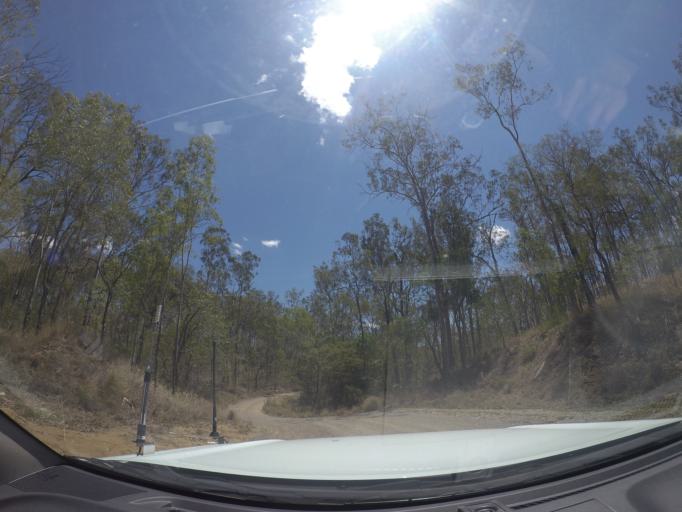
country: AU
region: Queensland
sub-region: Ipswich
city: Springfield Lakes
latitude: -27.8049
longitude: 152.8439
